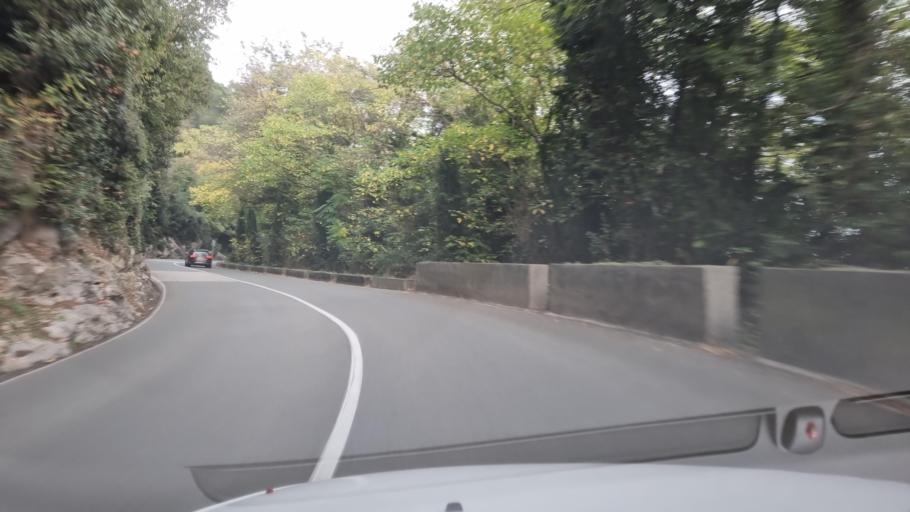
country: HR
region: Primorsko-Goranska
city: Matulji
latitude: 45.3566
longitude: 14.3274
